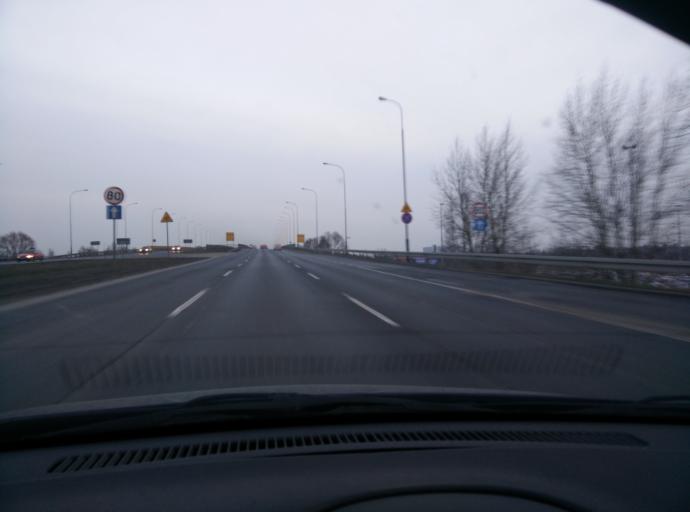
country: PL
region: Greater Poland Voivodeship
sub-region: Poznan
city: Poznan
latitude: 52.3756
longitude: 16.9827
